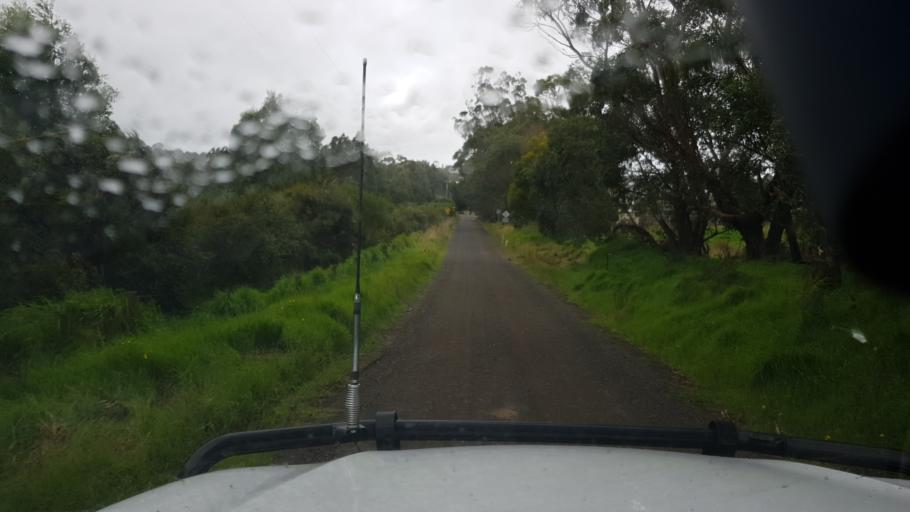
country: AU
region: Victoria
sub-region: Baw Baw
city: Warragul
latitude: -38.1403
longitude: 145.8390
